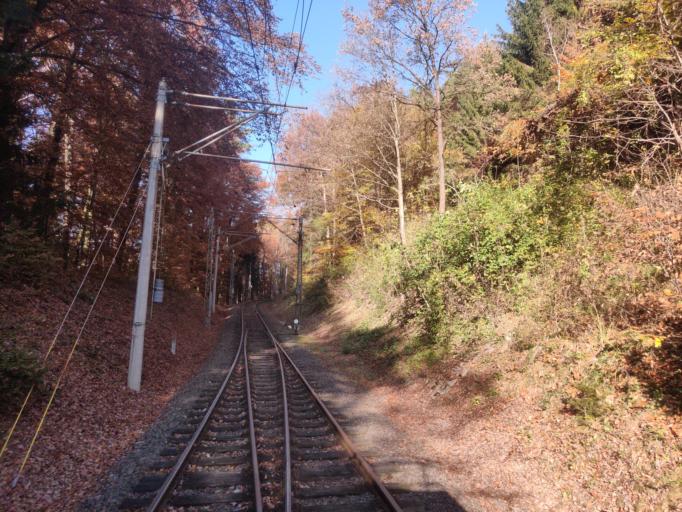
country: AT
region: Styria
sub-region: Politischer Bezirk Suedoststeiermark
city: Gnas
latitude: 46.8864
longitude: 15.8313
